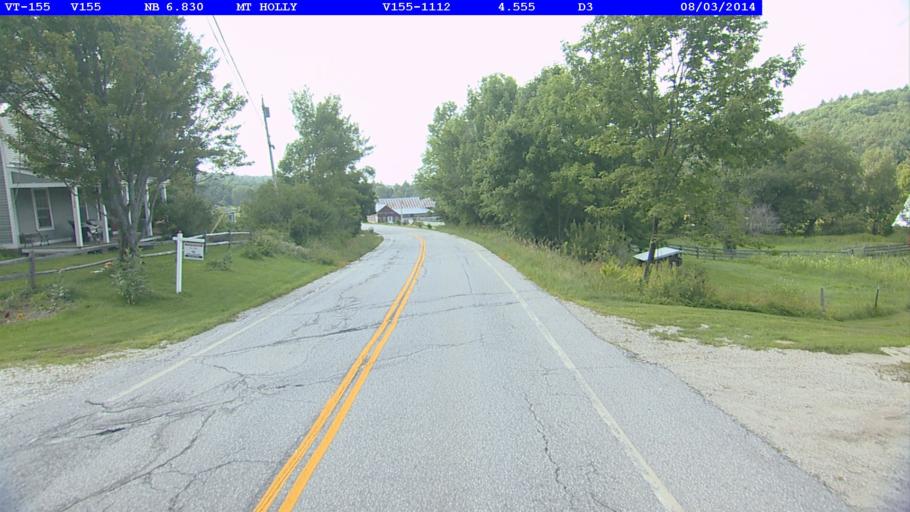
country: US
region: Vermont
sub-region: Rutland County
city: Rutland
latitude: 43.4114
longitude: -72.8445
